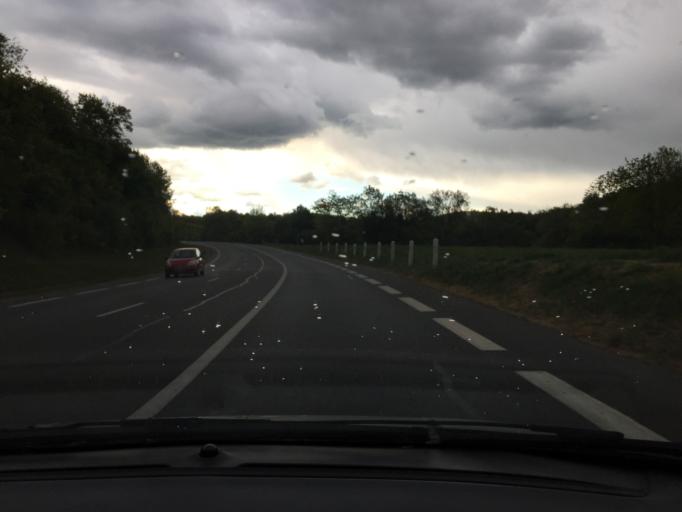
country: FR
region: Rhone-Alpes
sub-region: Departement du Rhone
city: Montagny
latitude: 45.6434
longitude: 4.7519
